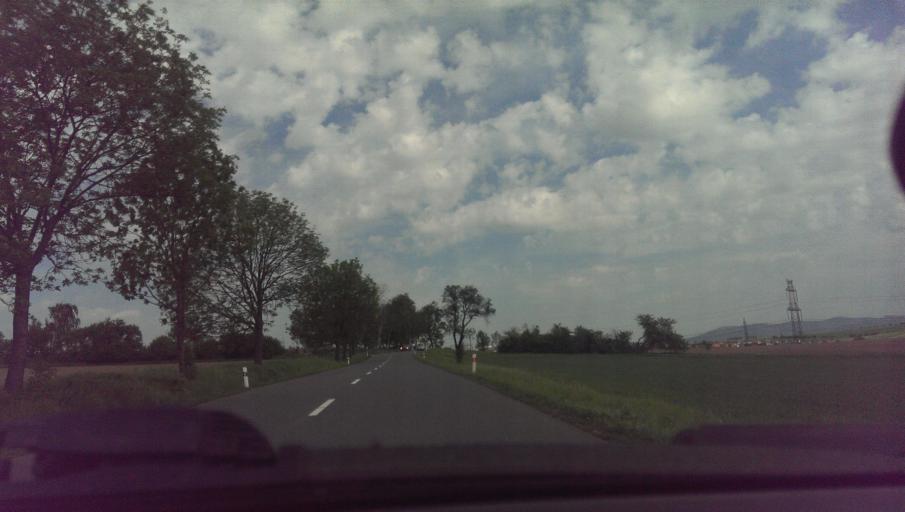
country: CZ
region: Zlin
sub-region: Okres Zlin
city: Otrokovice
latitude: 49.2423
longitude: 17.5388
